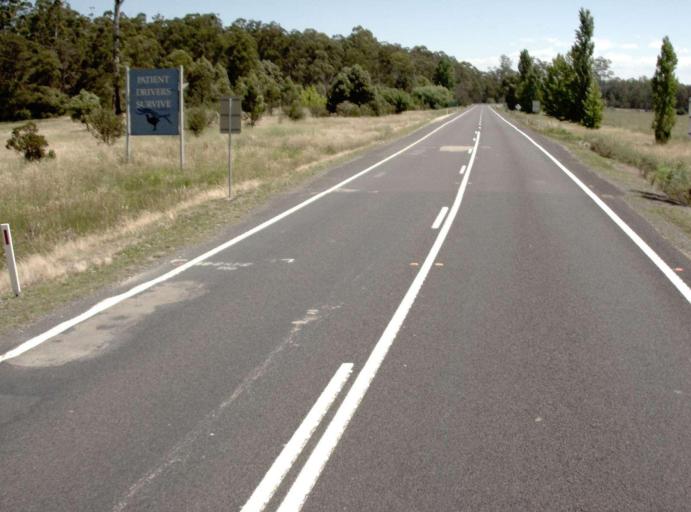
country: AU
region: New South Wales
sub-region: Bombala
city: Bombala
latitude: -37.5670
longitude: 149.1432
